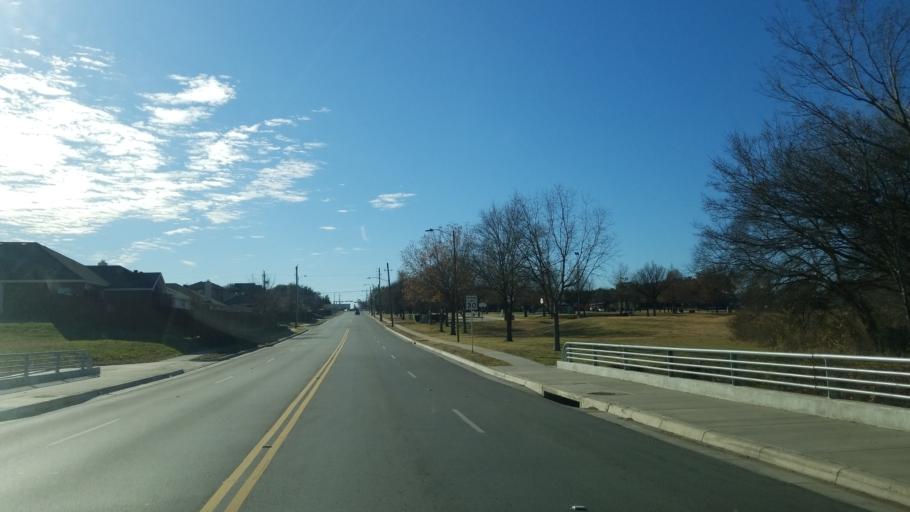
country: US
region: Texas
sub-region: Tarrant County
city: Arlington
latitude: 32.7247
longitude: -97.0572
